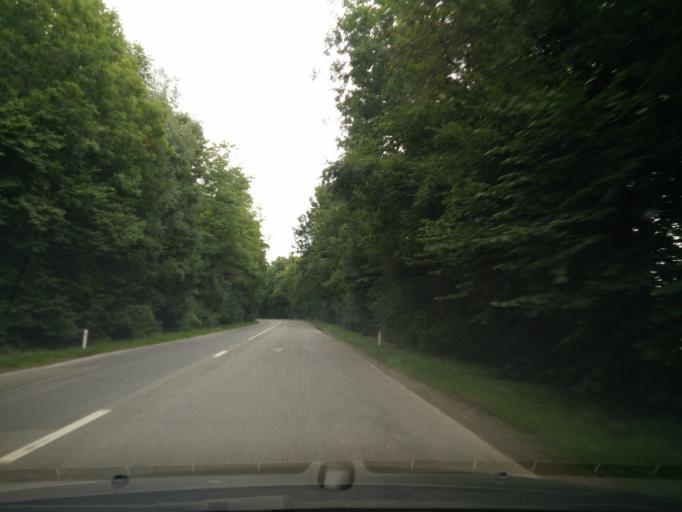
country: BE
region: Wallonia
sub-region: Province de Liege
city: Oupeye
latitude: 50.7464
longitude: 5.6589
